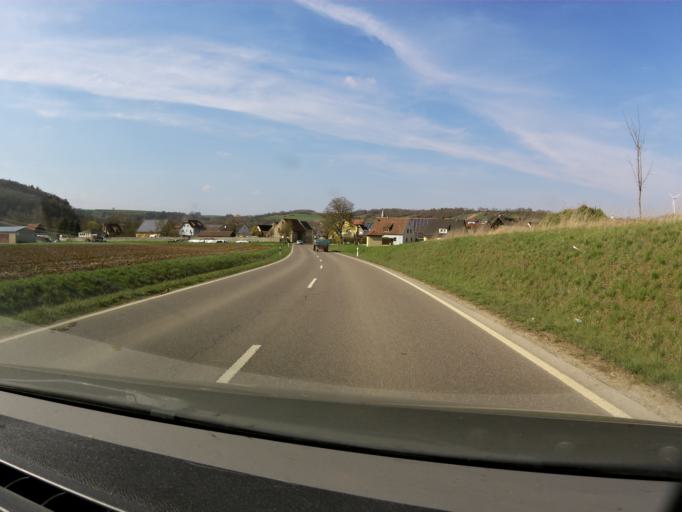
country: DE
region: Bavaria
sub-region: Regierungsbezirk Unterfranken
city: Bieberehren
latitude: 49.5119
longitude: 10.0102
